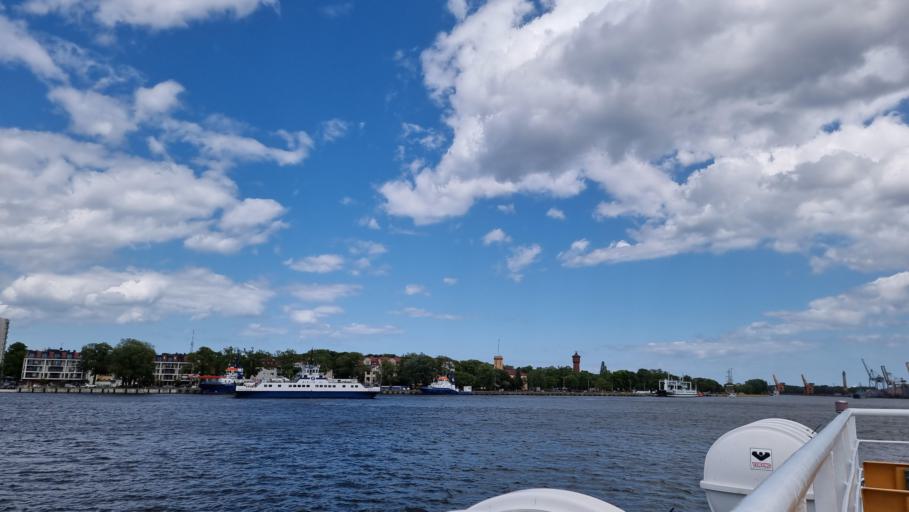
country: PL
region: West Pomeranian Voivodeship
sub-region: Swinoujscie
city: Swinoujscie
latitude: 53.9047
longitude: 14.2597
